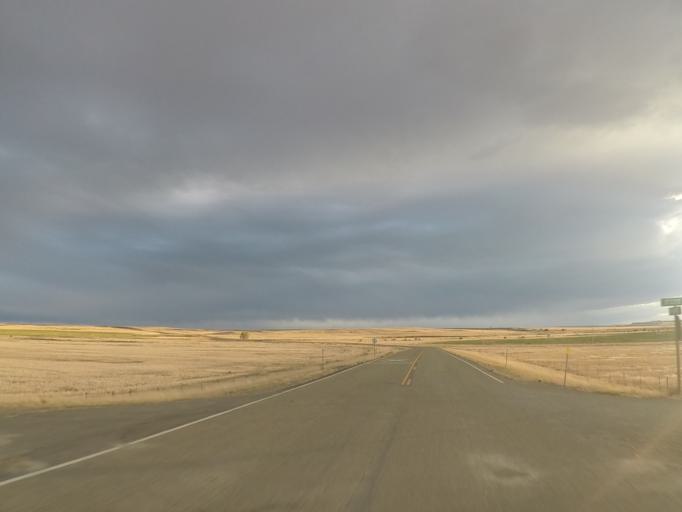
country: US
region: Montana
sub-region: Golden Valley County
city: Ryegate
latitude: 46.3695
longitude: -109.2658
